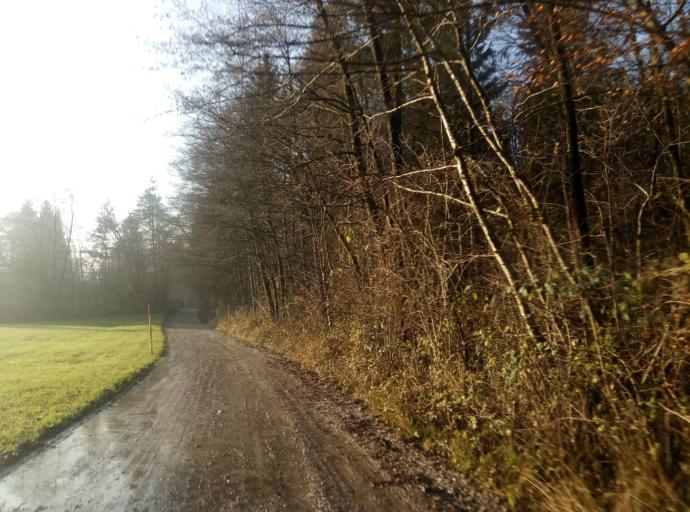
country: SI
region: Medvode
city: Zgornje Pirnice
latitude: 46.1326
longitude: 14.4751
